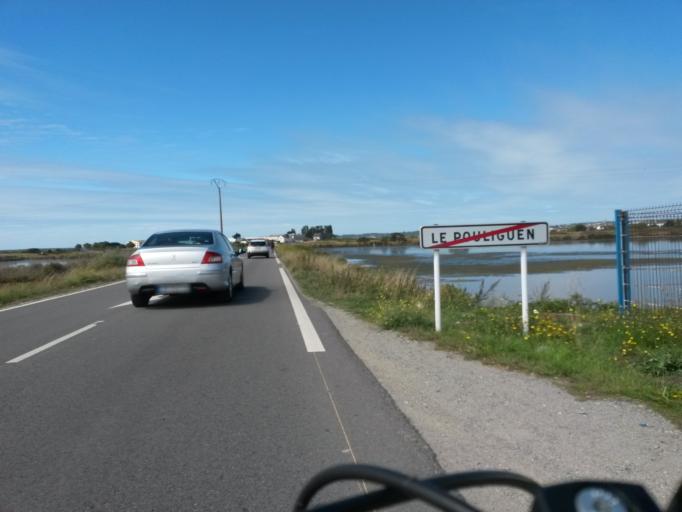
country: FR
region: Pays de la Loire
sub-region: Departement de la Loire-Atlantique
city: Le Pouliguen
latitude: 47.2832
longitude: -2.4343
